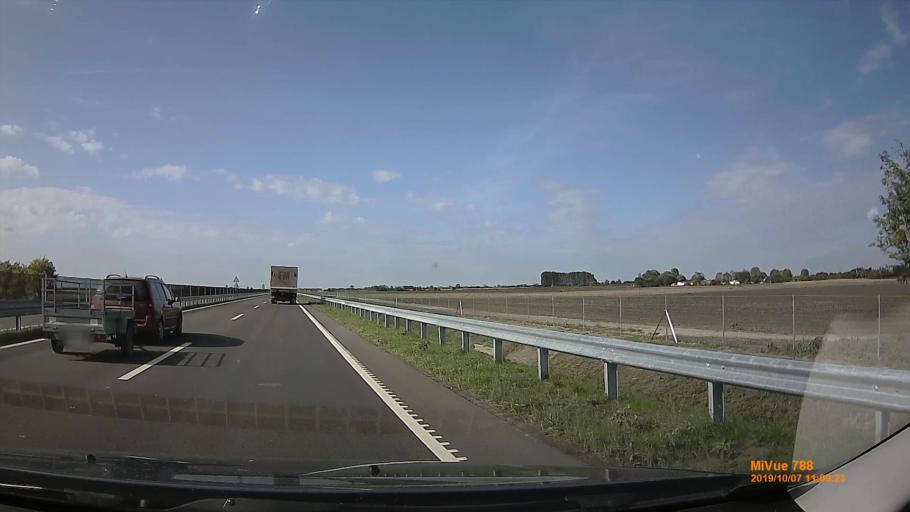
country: HU
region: Bekes
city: Kondoros
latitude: 46.7435
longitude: 20.8364
